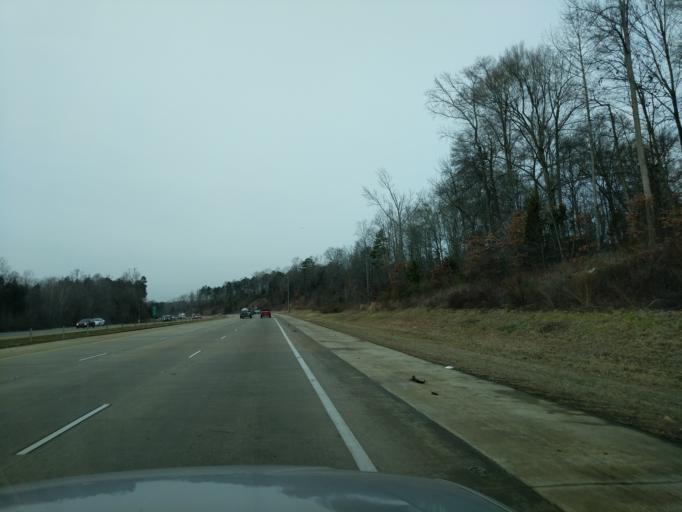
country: US
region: North Carolina
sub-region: Mecklenburg County
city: Huntersville
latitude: 35.3401
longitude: -80.8971
